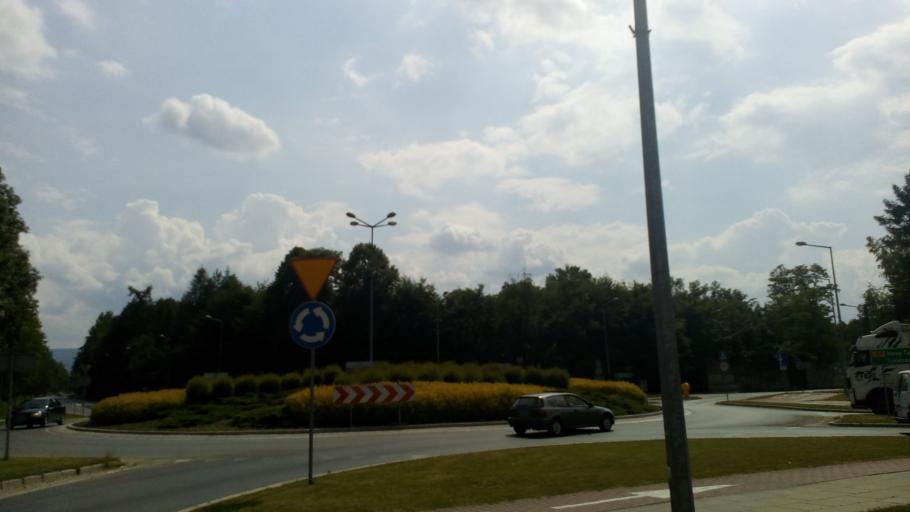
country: PL
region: Lesser Poland Voivodeship
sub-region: Powiat nowosadecki
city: Stary Sacz
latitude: 49.5675
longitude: 20.6570
